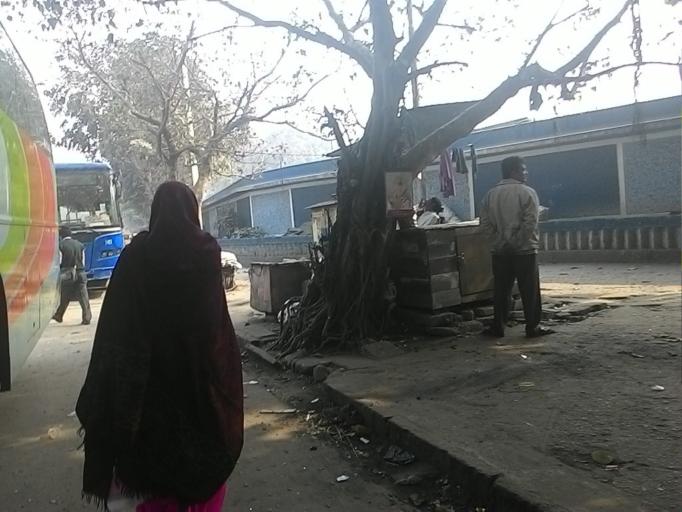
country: IN
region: West Bengal
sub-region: Kolkata
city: Bara Bazar
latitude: 22.5618
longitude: 88.3498
